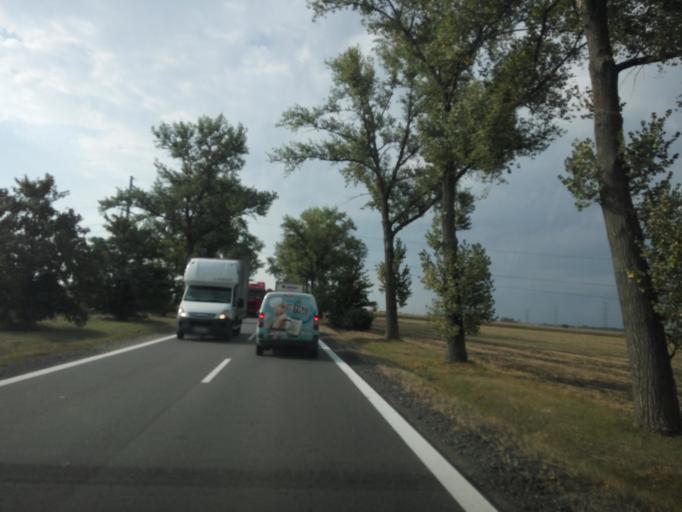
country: PL
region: Lower Silesian Voivodeship
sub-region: Powiat wroclawski
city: Zerniki Wroclawskie
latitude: 51.0086
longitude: 17.0645
